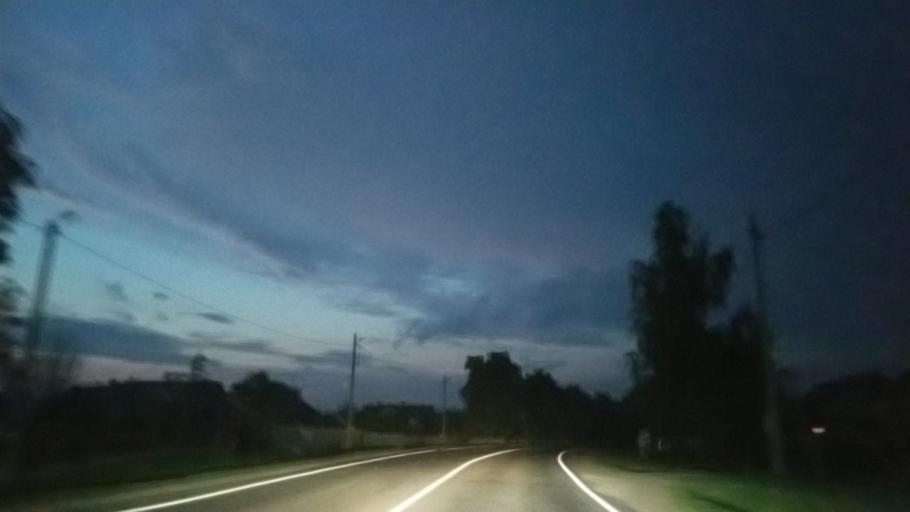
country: PL
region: Lublin Voivodeship
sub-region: Powiat bialski
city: Koden
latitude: 51.9330
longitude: 23.6594
